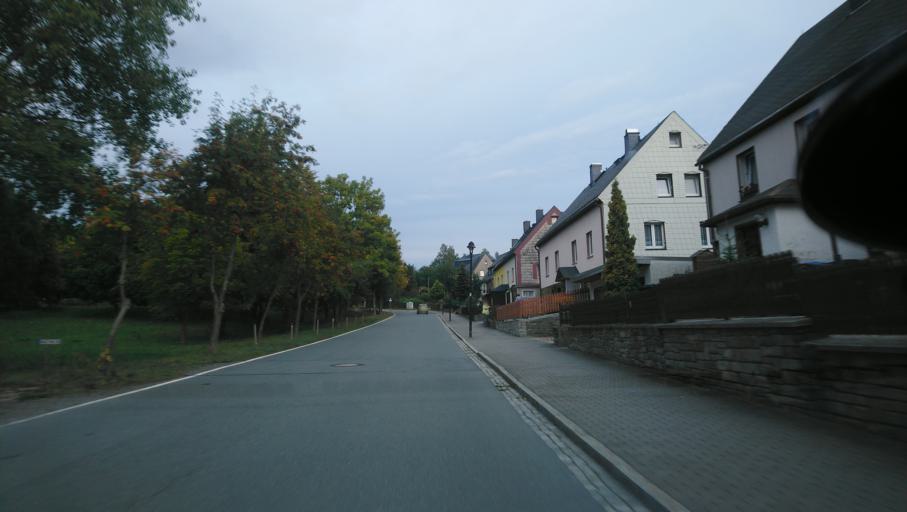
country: DE
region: Saxony
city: Barenstein
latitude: 50.5312
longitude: 13.0005
